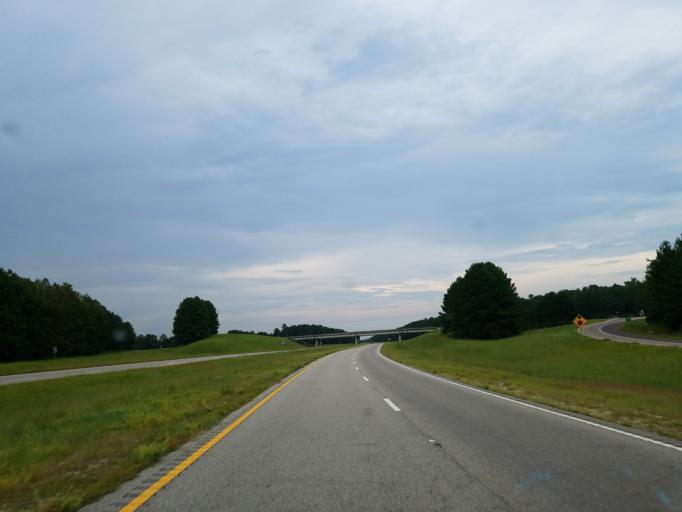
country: US
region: Mississippi
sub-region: Lauderdale County
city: Meridian
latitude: 32.3001
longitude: -88.6927
